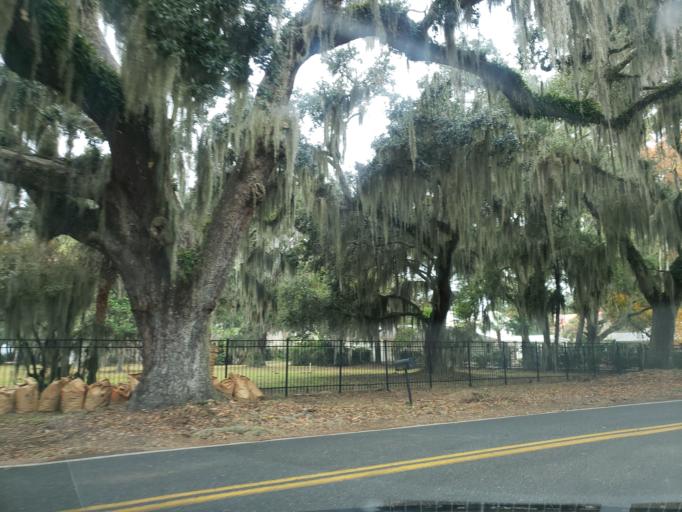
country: US
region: Georgia
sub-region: Chatham County
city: Wilmington Island
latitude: 31.9794
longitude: -80.9982
